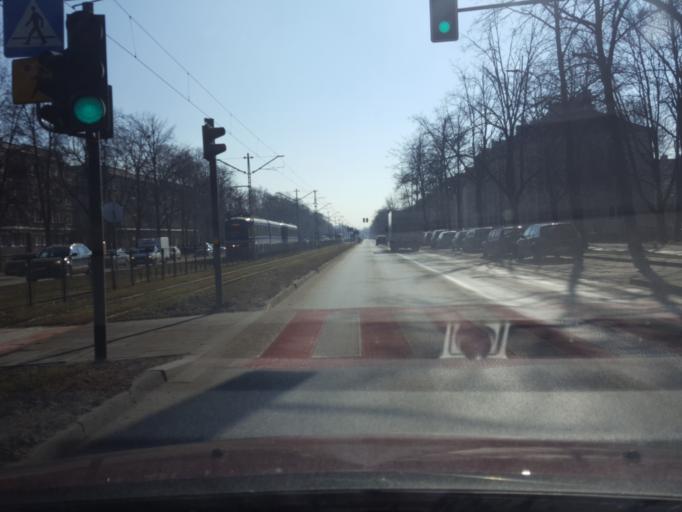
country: PL
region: Lesser Poland Voivodeship
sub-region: Powiat wielicki
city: Kokotow
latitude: 50.0702
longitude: 20.0431
